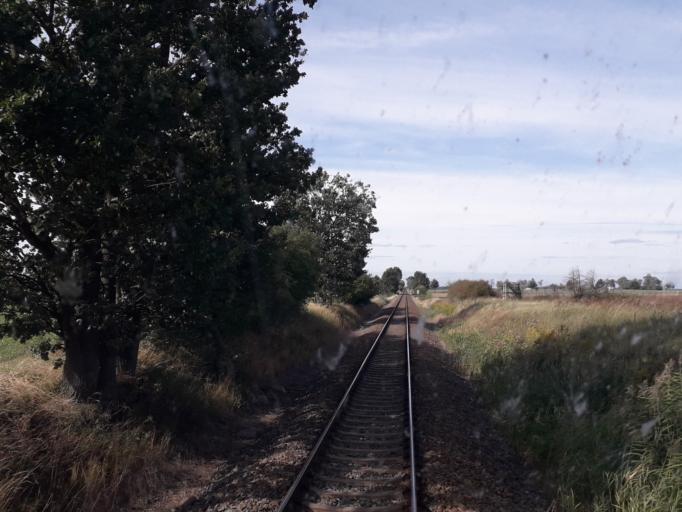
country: DE
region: Brandenburg
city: Neuruppin
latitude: 52.8851
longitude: 12.8525
